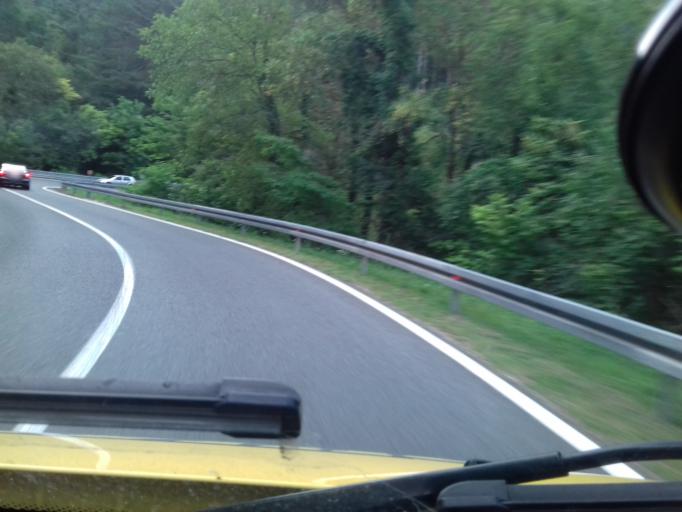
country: BA
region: Federation of Bosnia and Herzegovina
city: Ostrozac
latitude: 44.9014
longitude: 15.9367
